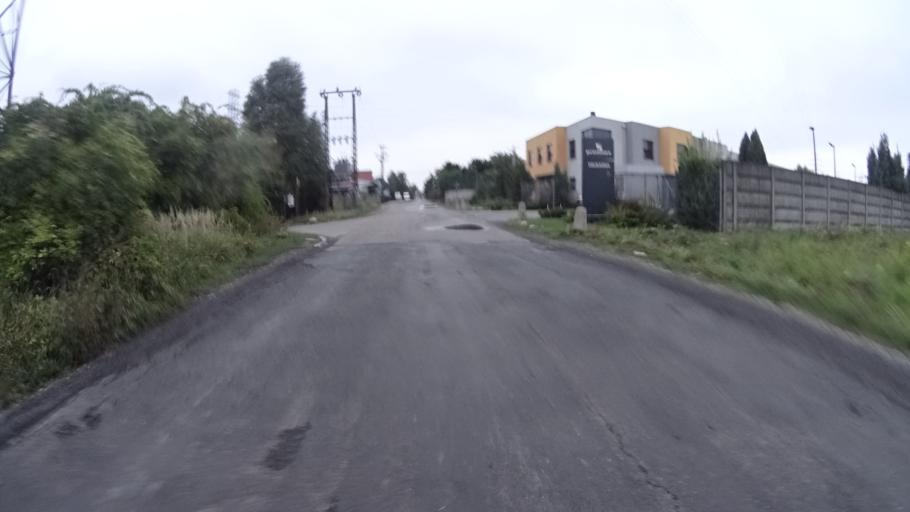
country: PL
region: Masovian Voivodeship
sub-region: Warszawa
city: Ursus
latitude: 52.2207
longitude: 20.8795
